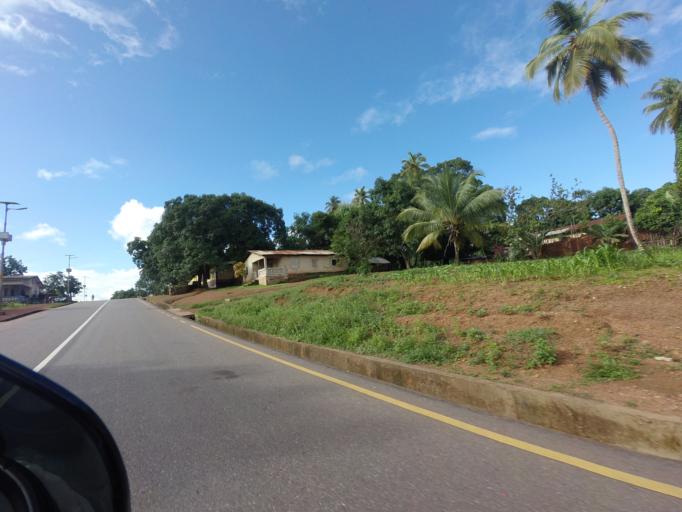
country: SL
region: Northern Province
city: Kambia
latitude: 9.1246
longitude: -12.9177
